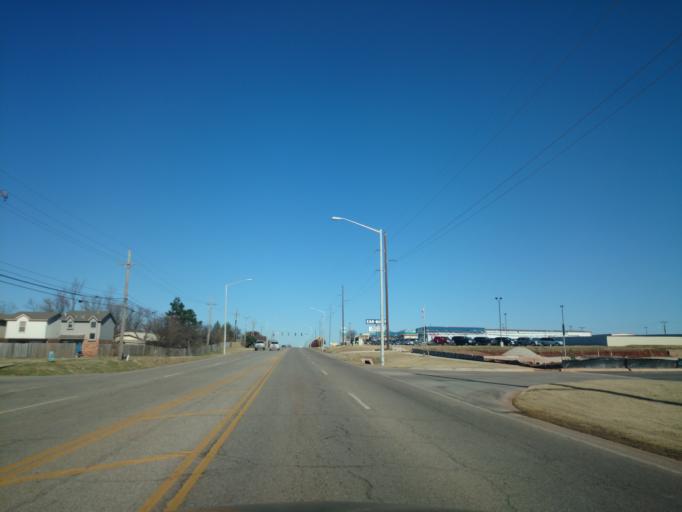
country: US
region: Oklahoma
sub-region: Payne County
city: Stillwater
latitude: 36.1460
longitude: -97.0516
